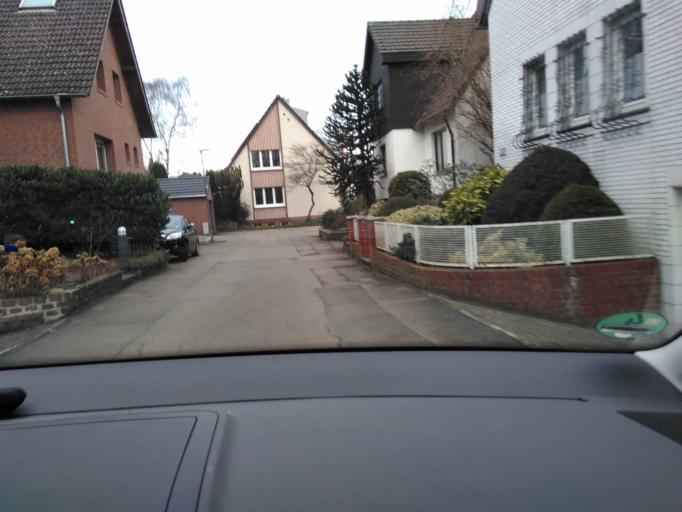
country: DE
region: North Rhine-Westphalia
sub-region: Regierungsbezirk Koln
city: Aachen
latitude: 50.7936
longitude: 6.0629
